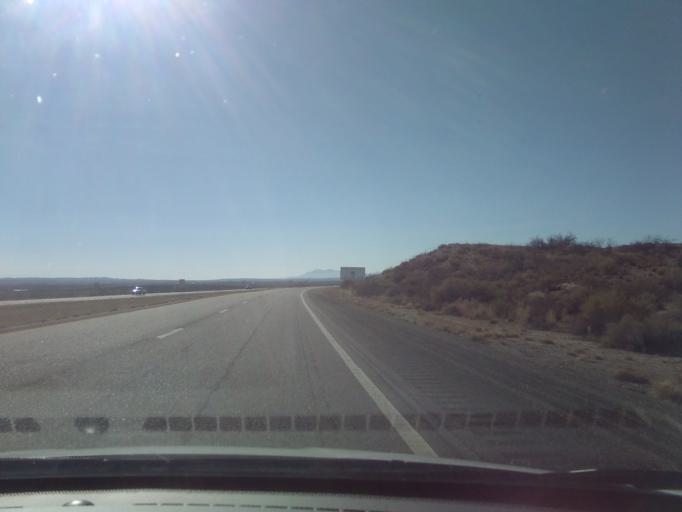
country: US
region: New Mexico
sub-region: Valencia County
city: Jarales
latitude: 34.4287
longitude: -106.8324
